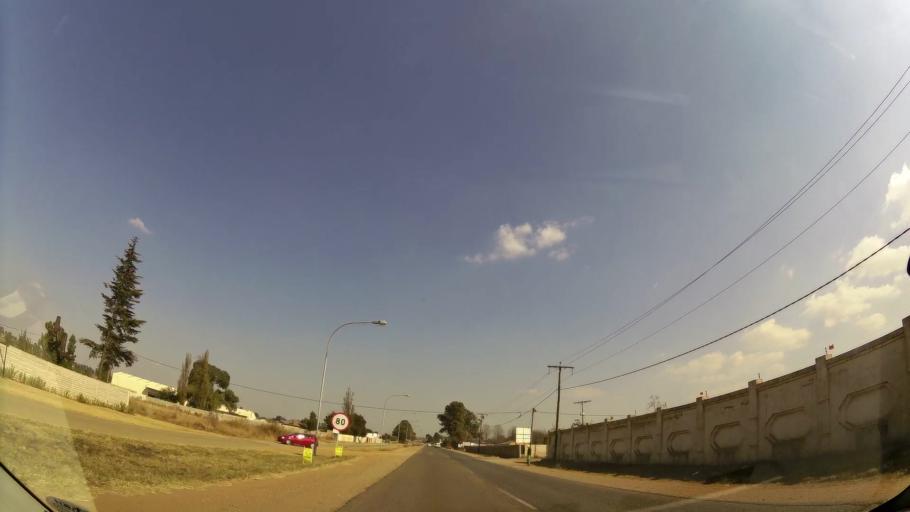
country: ZA
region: Gauteng
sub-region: Ekurhuleni Metropolitan Municipality
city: Benoni
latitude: -26.1201
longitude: 28.4010
